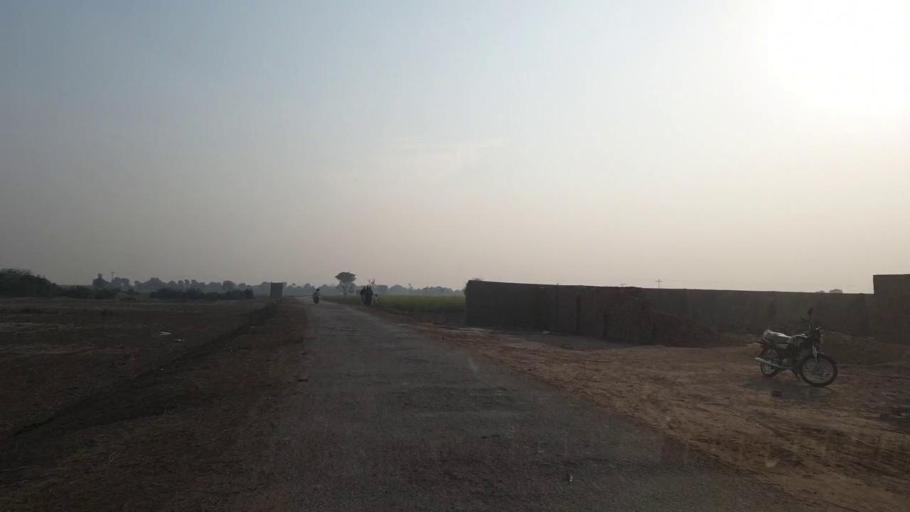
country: PK
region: Sindh
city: Bhit Shah
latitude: 25.8070
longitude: 68.4648
